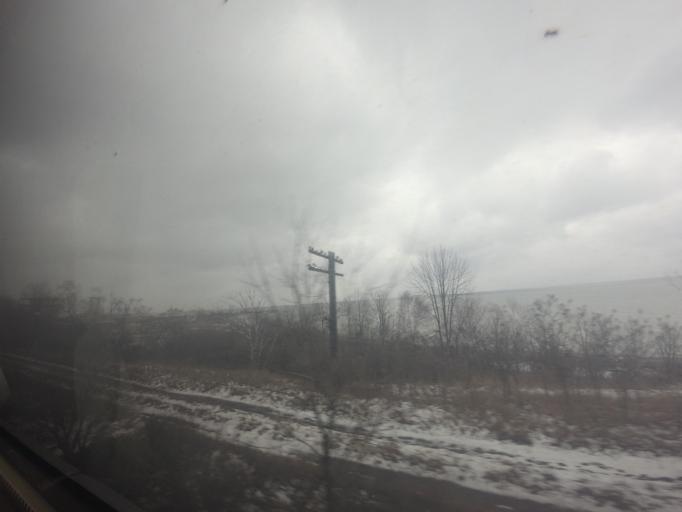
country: CA
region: Ontario
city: Cobourg
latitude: 43.9417
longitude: -78.3017
